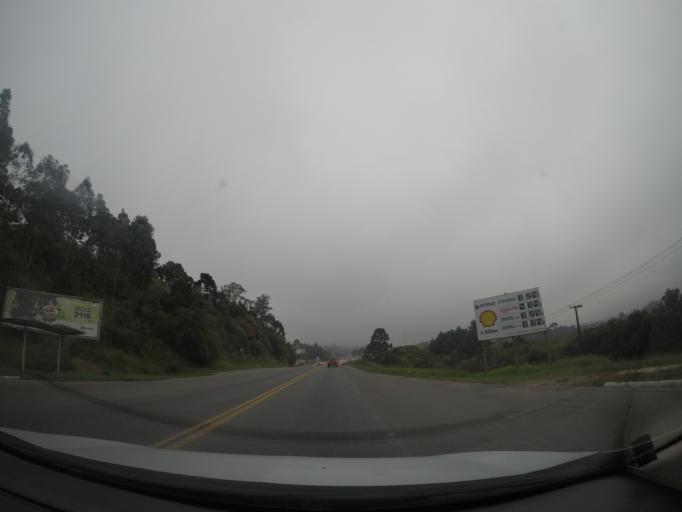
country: BR
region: Parana
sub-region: Almirante Tamandare
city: Almirante Tamandare
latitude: -25.3250
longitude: -49.2968
